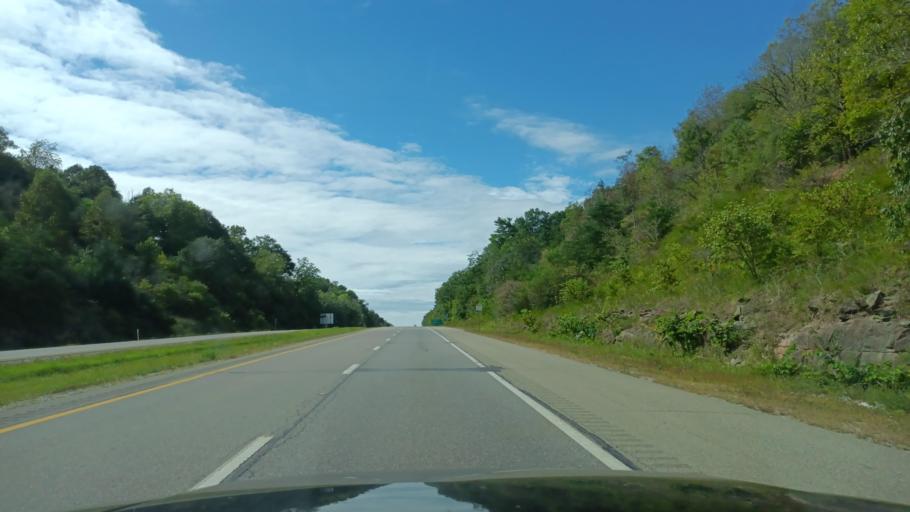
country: US
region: West Virginia
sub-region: Ritchie County
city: Pennsboro
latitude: 39.2742
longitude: -80.9971
